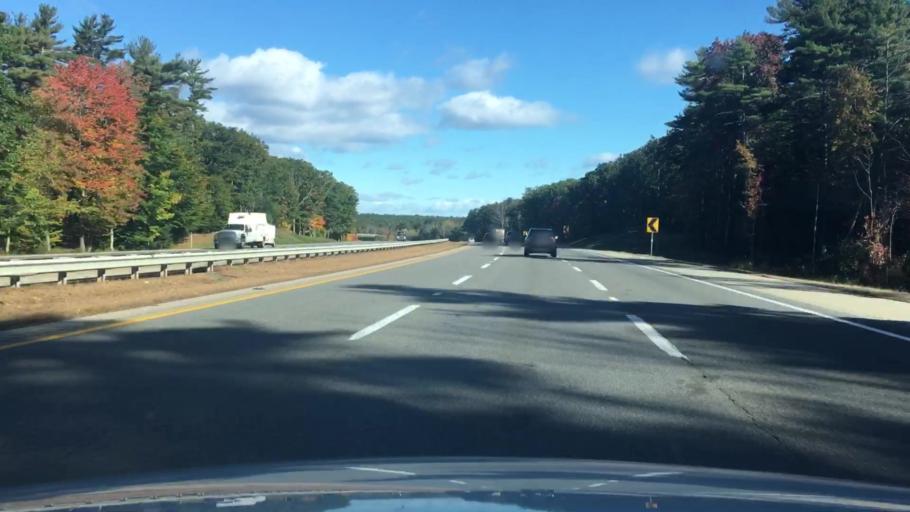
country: US
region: Maine
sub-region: York County
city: Ogunquit
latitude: 43.2550
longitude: -70.6211
